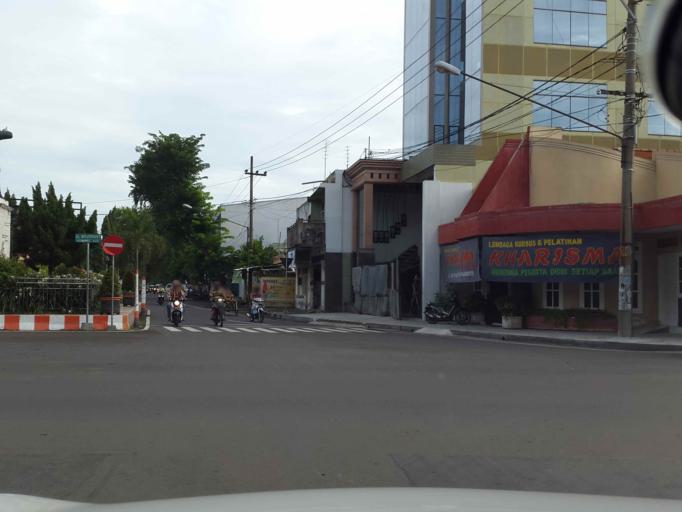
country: ID
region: East Java
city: Soko
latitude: -7.4809
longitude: 112.4321
